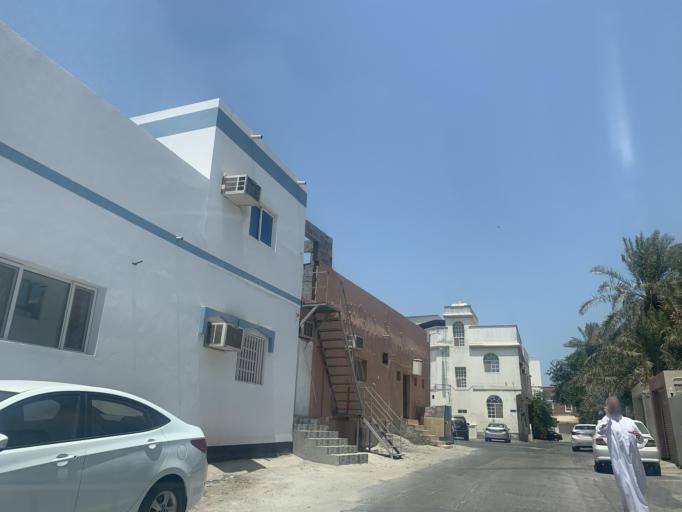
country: BH
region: Muharraq
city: Al Muharraq
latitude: 26.2842
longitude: 50.6223
